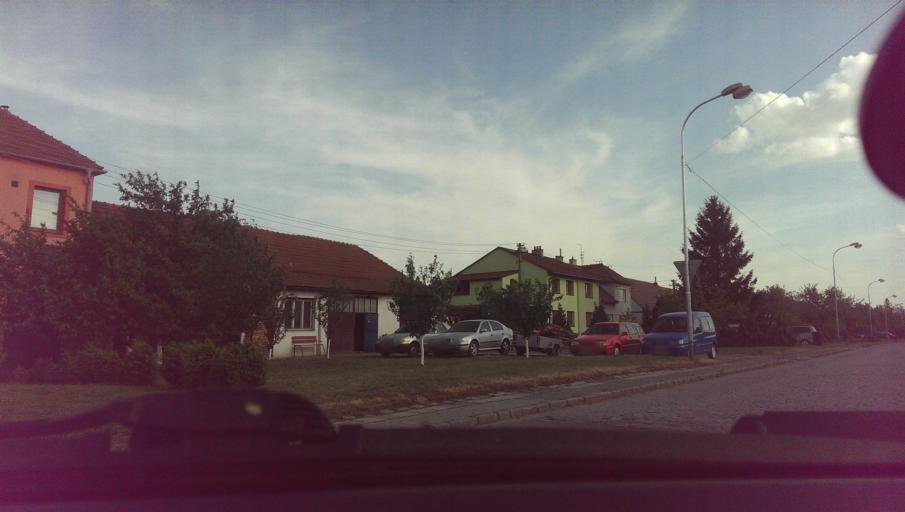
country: CZ
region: Zlin
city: Uhersky Brod
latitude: 49.0205
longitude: 17.6451
